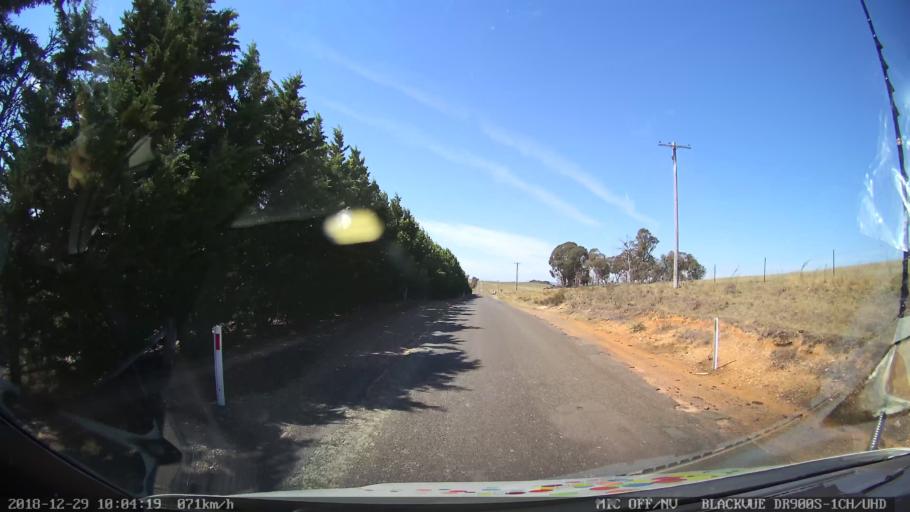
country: AU
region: New South Wales
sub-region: Goulburn Mulwaree
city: Goulburn
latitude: -34.8207
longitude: 149.4556
